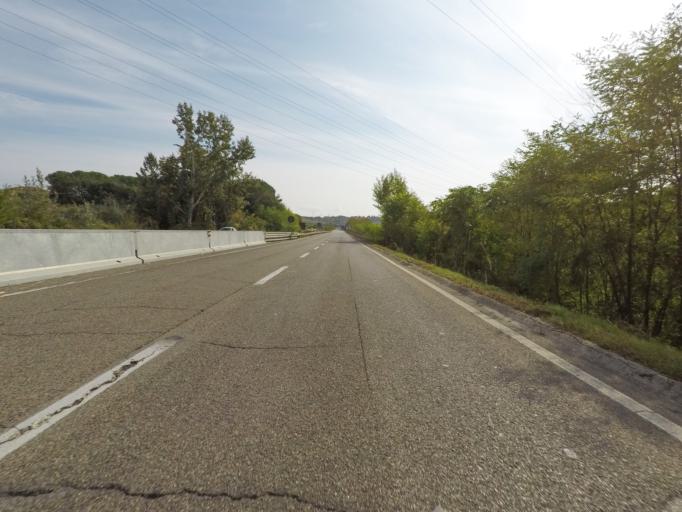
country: IT
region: Tuscany
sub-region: Provincia di Siena
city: Siena
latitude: 43.2979
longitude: 11.3296
